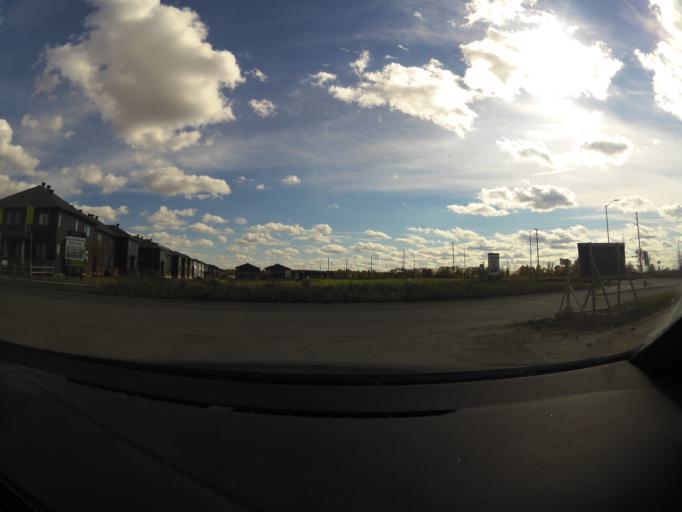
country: CA
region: Ontario
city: Bells Corners
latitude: 45.2688
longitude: -75.8897
